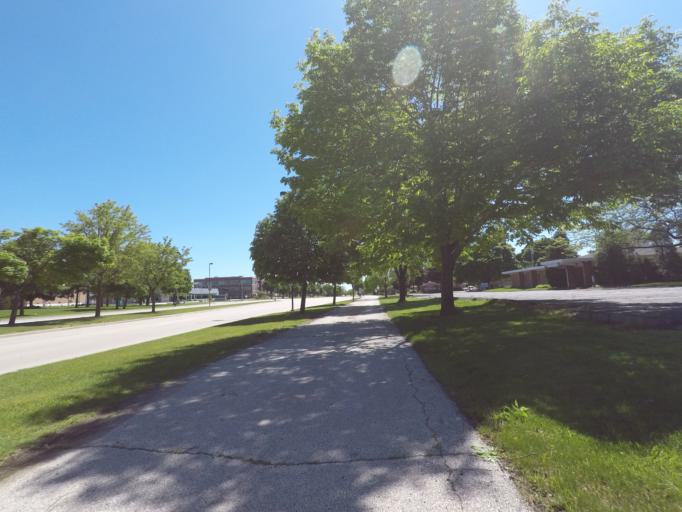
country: US
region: Wisconsin
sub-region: Sheboygan County
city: Sheboygan
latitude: 43.7562
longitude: -87.7383
